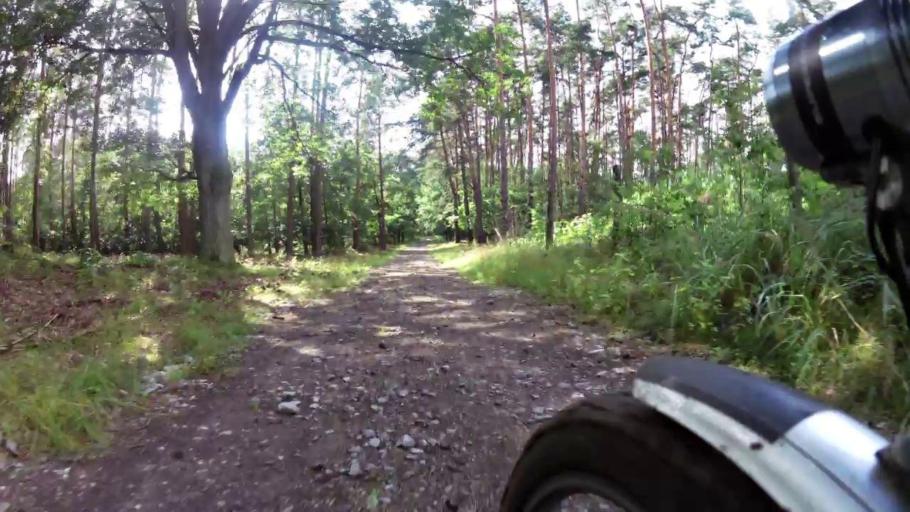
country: PL
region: West Pomeranian Voivodeship
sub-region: Powiat gryfinski
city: Gryfino
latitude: 53.1998
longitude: 14.5850
